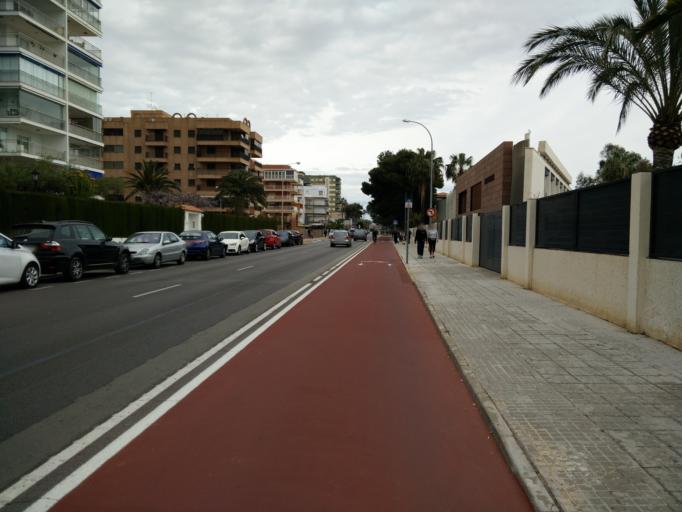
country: ES
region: Valencia
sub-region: Provincia de Castello
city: Benicassim
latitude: 40.0396
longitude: 0.0548
